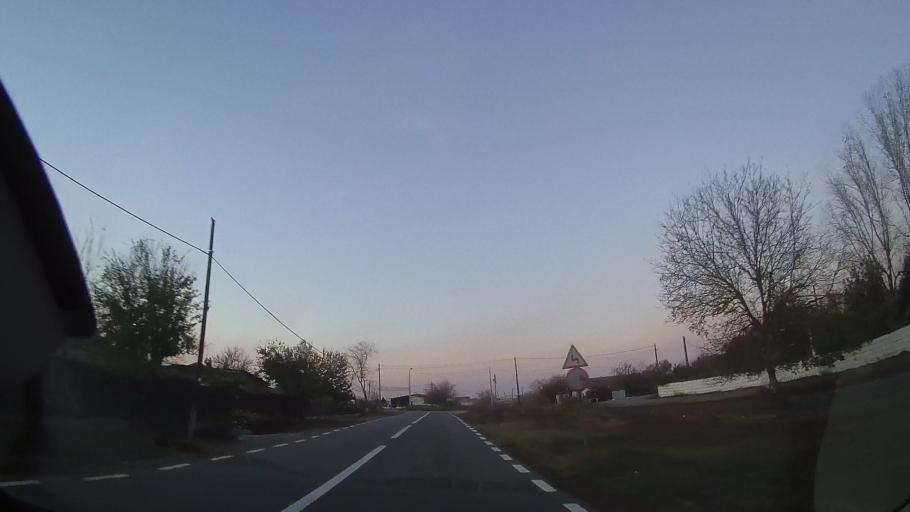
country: RO
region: Constanta
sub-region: Comuna Cobadin
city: Cobadin
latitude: 44.0545
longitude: 28.2464
